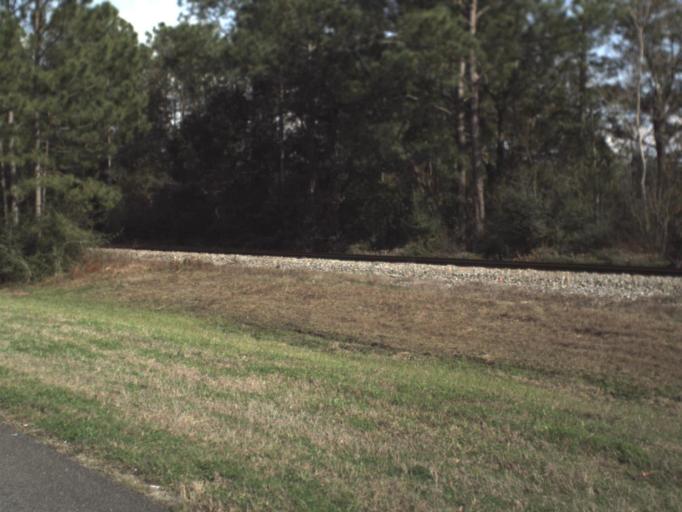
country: US
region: Florida
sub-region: Bay County
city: Hiland Park
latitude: 30.2447
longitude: -85.5627
